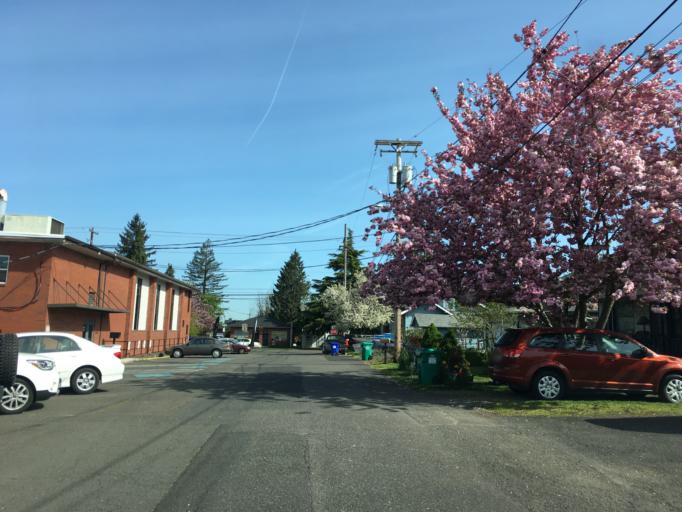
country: US
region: Oregon
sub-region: Multnomah County
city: Lents
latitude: 45.5256
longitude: -122.5702
